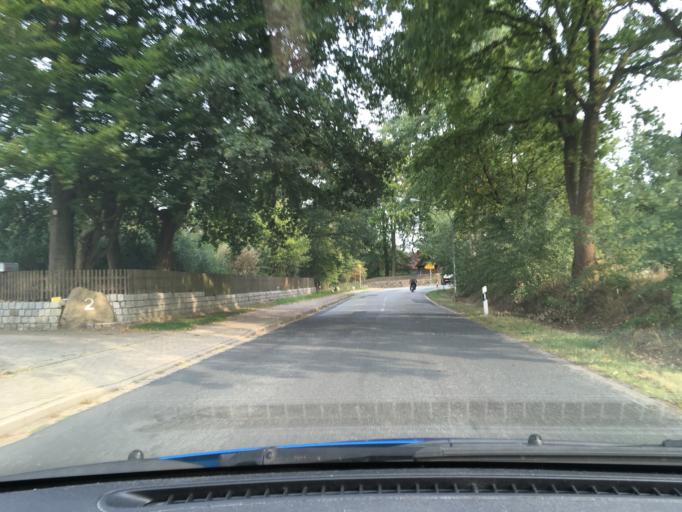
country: DE
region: Lower Saxony
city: Asendorf
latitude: 53.2685
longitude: 9.9784
